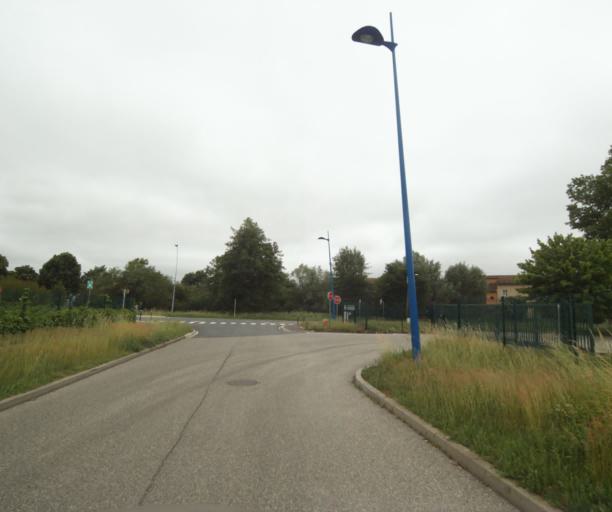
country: FR
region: Rhone-Alpes
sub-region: Departement de l'Ain
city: Mionnay
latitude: 45.8713
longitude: 4.9202
